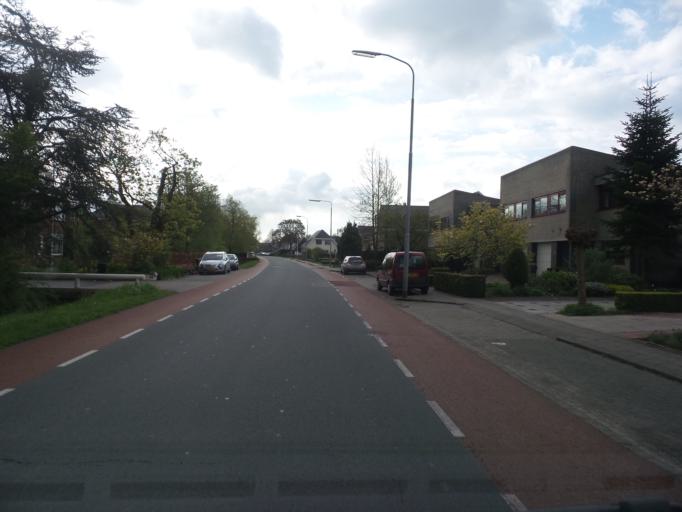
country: NL
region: South Holland
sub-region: Bodegraven-Reeuwijk
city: Bodegraven
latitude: 52.0821
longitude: 4.7586
